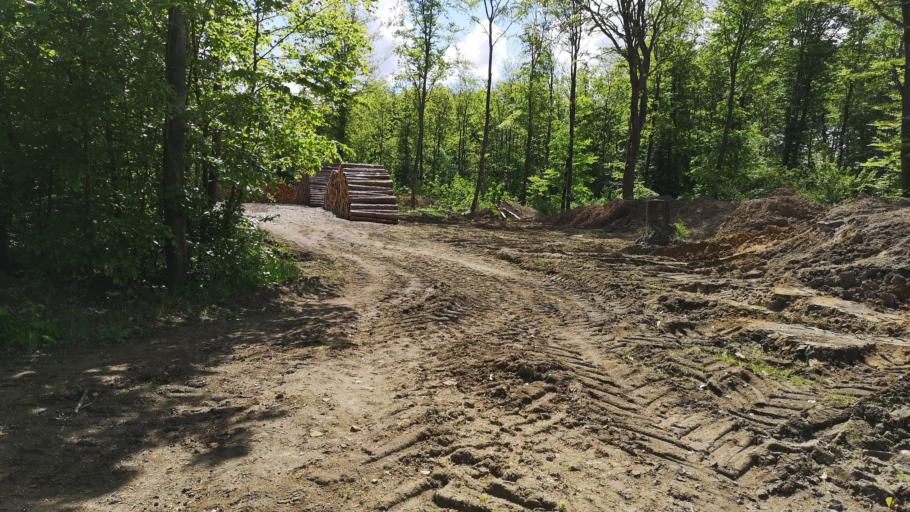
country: DK
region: South Denmark
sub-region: Kolding Kommune
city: Lunderskov
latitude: 55.5211
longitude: 9.2582
